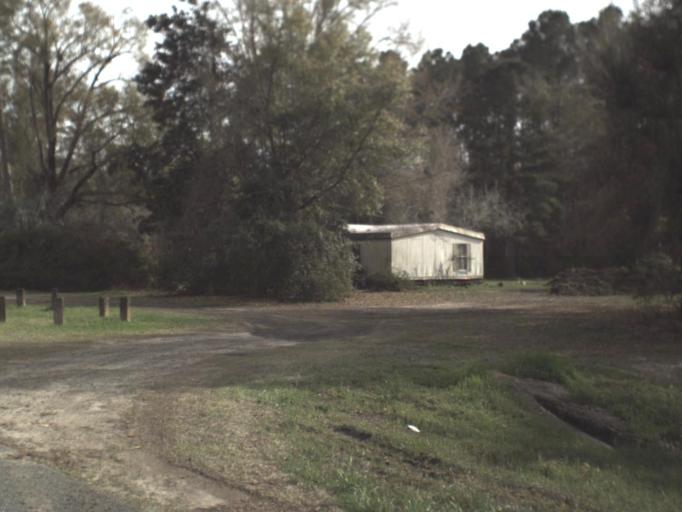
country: US
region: Florida
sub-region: Jefferson County
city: Monticello
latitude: 30.5109
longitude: -83.7749
